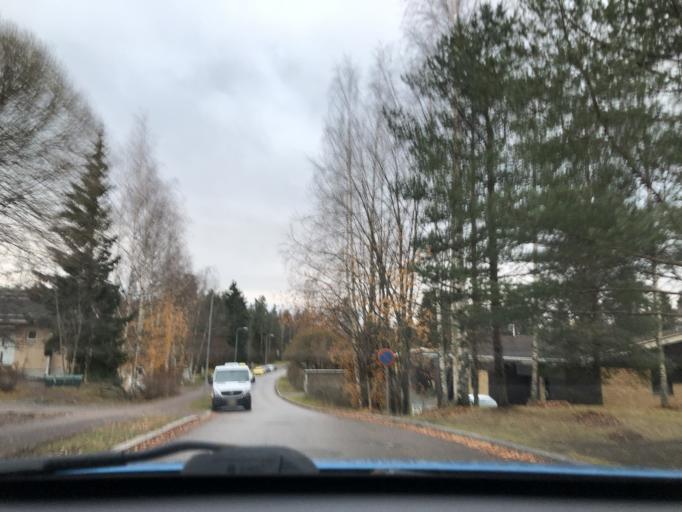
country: FI
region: Pirkanmaa
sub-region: Tampere
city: Kangasala
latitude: 61.5269
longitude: 23.9523
